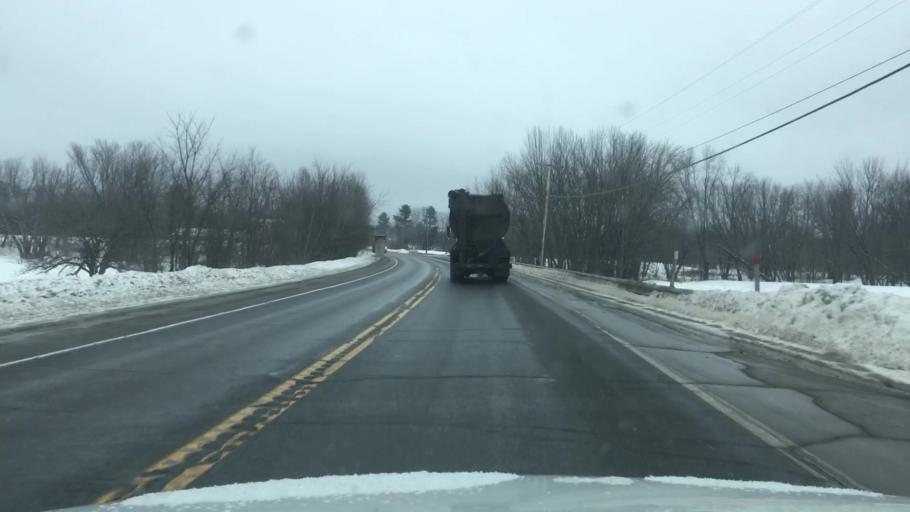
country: US
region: Maine
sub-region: Franklin County
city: New Sharon
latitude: 44.6385
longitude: -70.0432
